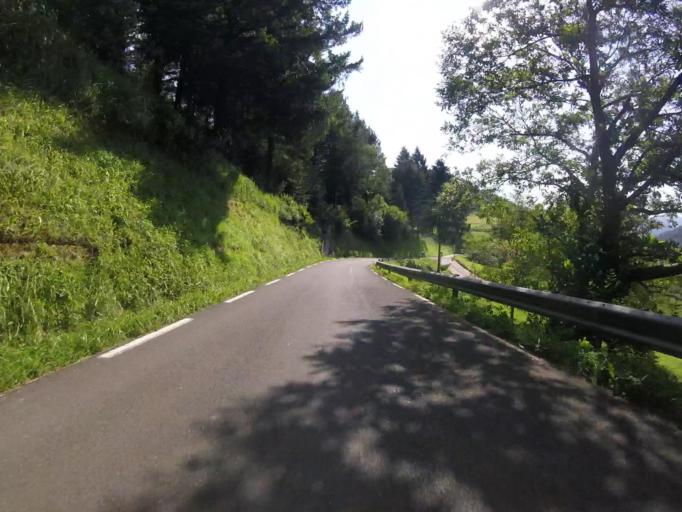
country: ES
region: Basque Country
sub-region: Provincia de Guipuzcoa
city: Alquiza
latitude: 43.1713
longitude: -2.1084
